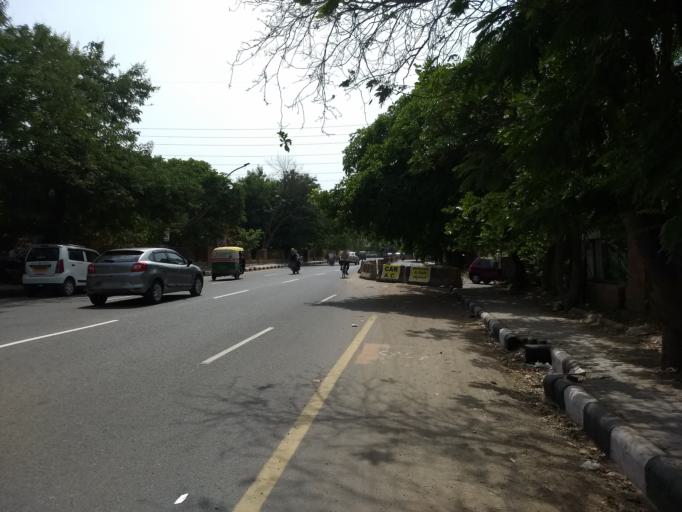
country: IN
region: Haryana
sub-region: Gurgaon
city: Gurgaon
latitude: 28.4680
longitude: 77.0747
